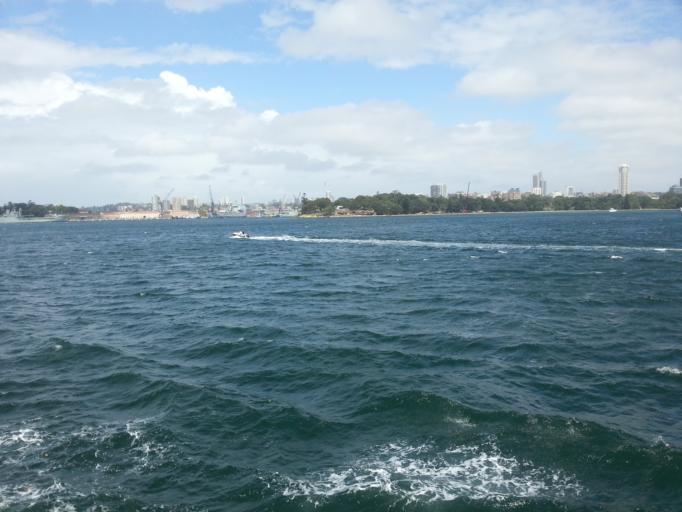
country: AU
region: New South Wales
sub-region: North Sydney
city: Kirribilli
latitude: -33.8535
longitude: 151.2177
